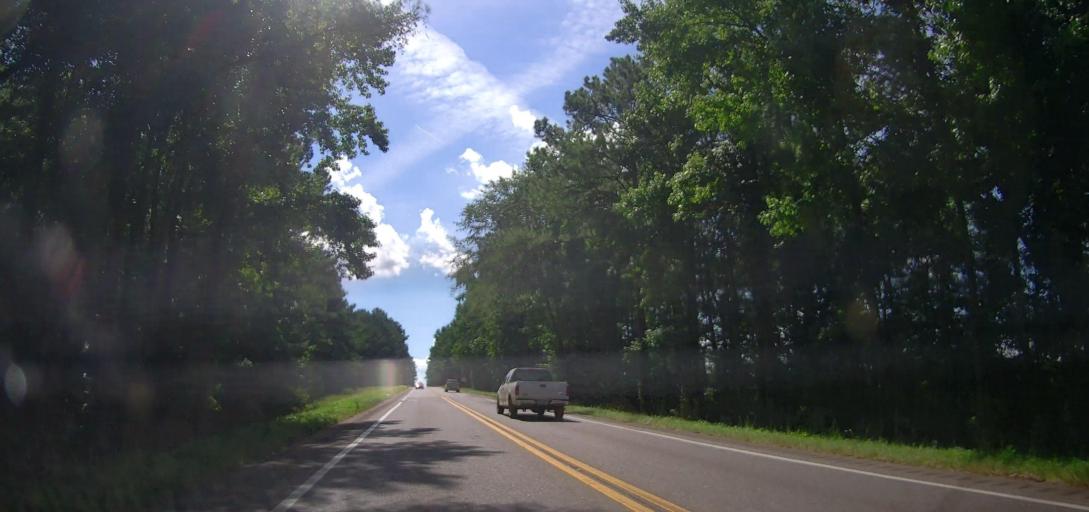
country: US
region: Alabama
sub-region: Pickens County
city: Gordo
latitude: 33.2844
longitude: -87.8400
